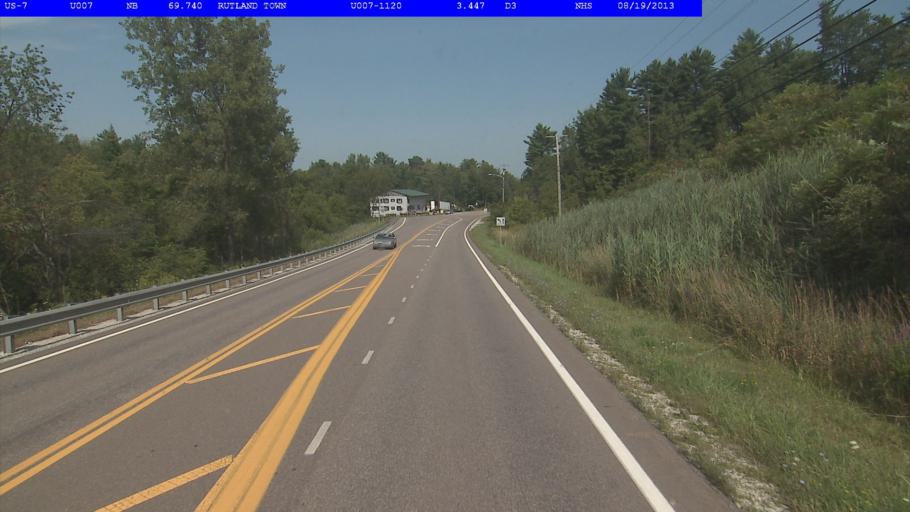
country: US
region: Vermont
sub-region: Rutland County
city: Rutland
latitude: 43.6598
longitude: -72.9894
